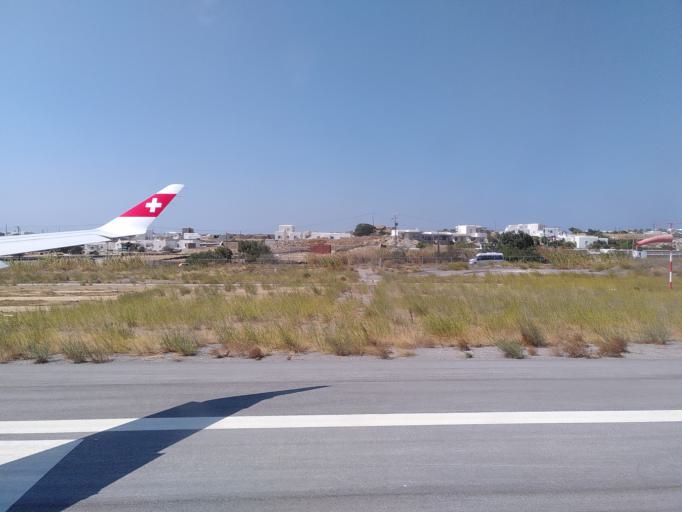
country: GR
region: South Aegean
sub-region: Nomos Kykladon
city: Mykonos
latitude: 37.4301
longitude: 25.3505
